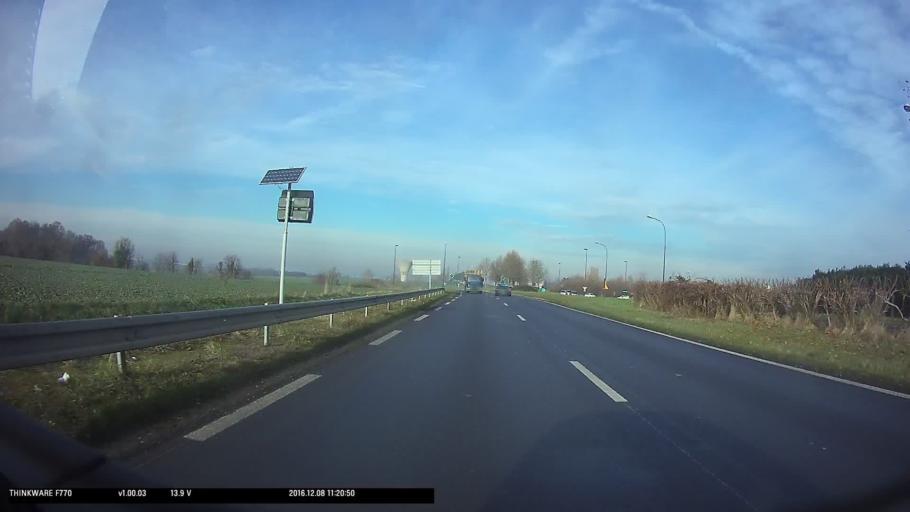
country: FR
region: Ile-de-France
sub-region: Departement du Val-d'Oise
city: Osny
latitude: 49.0788
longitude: 2.0726
